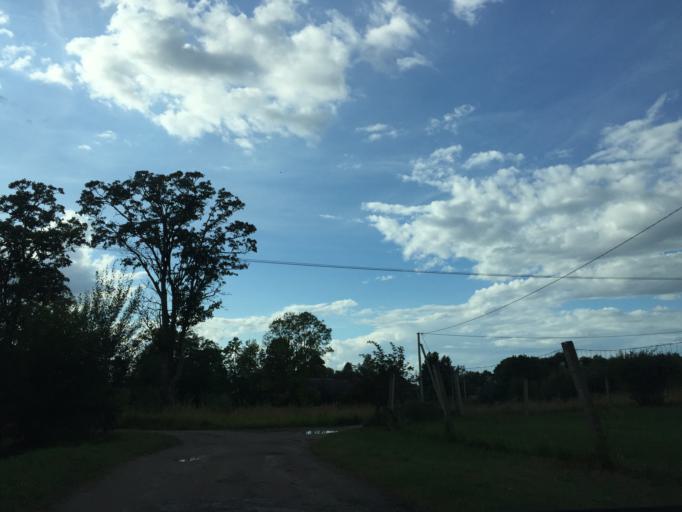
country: LT
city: Zagare
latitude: 56.3642
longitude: 23.2668
